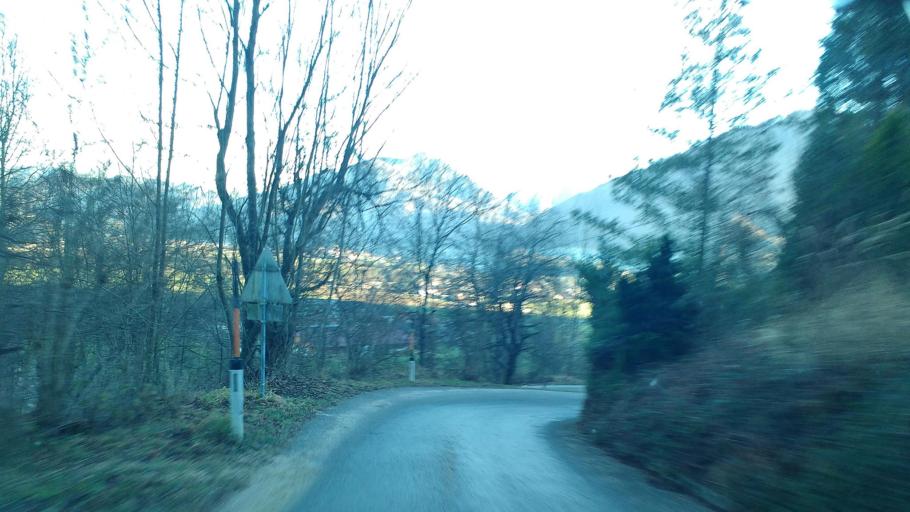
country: AT
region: Upper Austria
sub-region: Politischer Bezirk Kirchdorf an der Krems
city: Gruenburg
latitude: 47.8940
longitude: 14.2257
